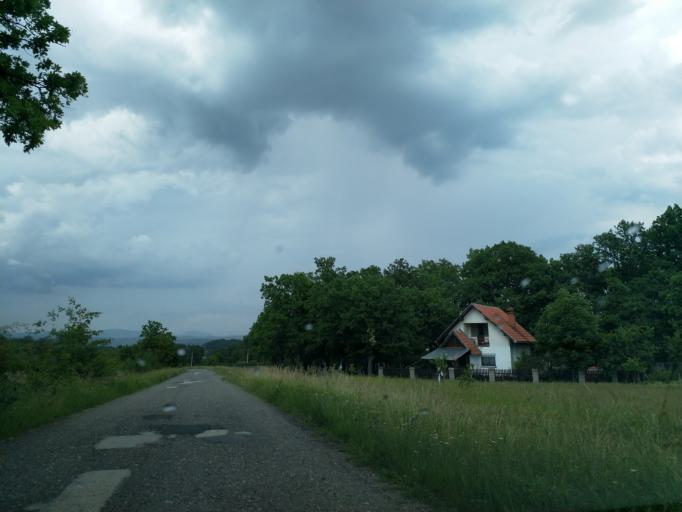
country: RS
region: Central Serbia
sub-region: Zajecarski Okrug
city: Boljevac
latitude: 43.9671
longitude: 21.9681
